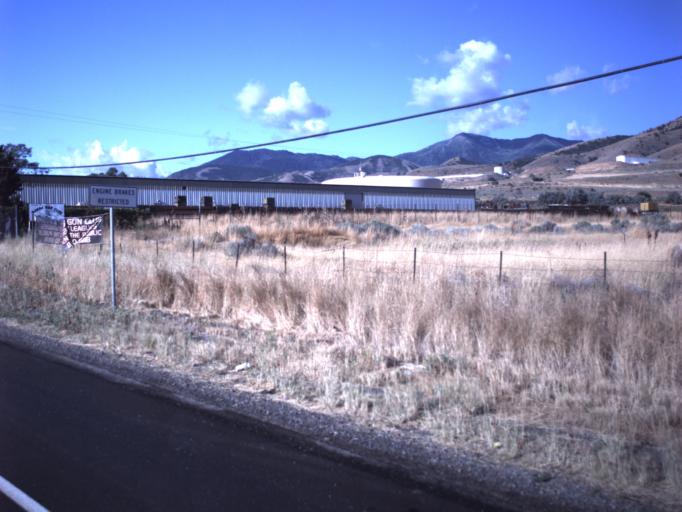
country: US
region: Utah
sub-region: Salt Lake County
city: Magna
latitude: 40.6846
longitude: -112.0919
